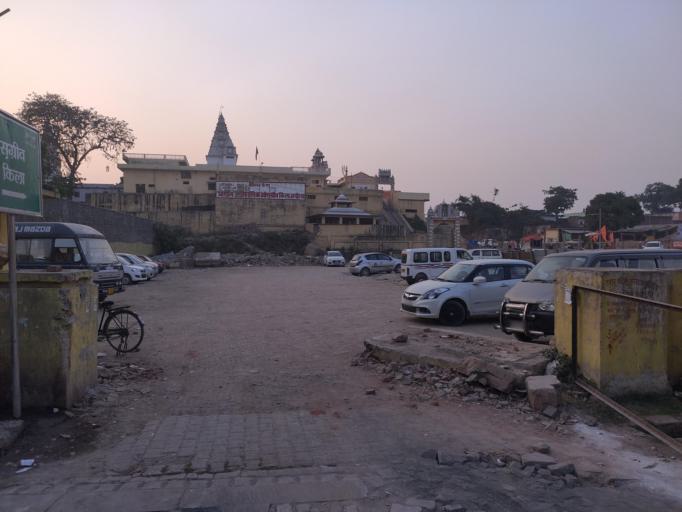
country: IN
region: Uttar Pradesh
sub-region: Faizabad
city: Ayodhya
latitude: 26.7930
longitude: 82.2006
